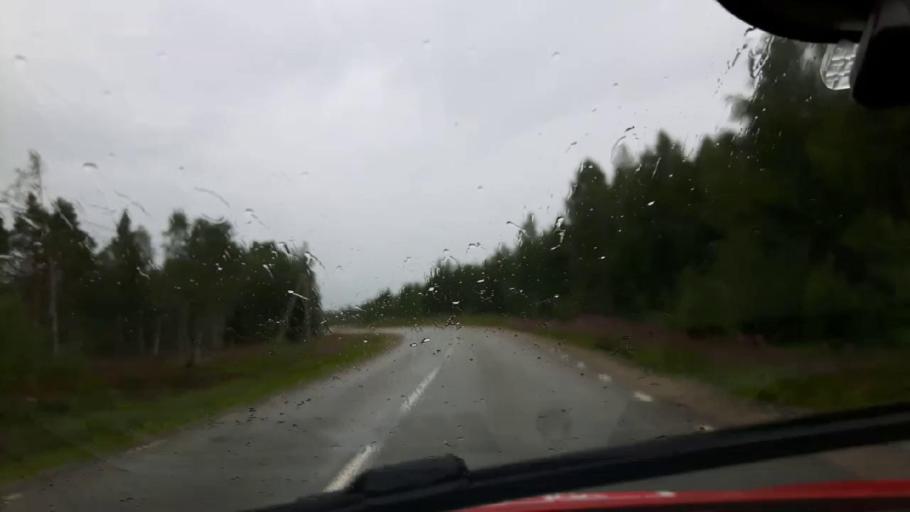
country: SE
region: Jaemtland
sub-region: OEstersunds Kommun
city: Brunflo
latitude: 62.7931
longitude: 15.0040
